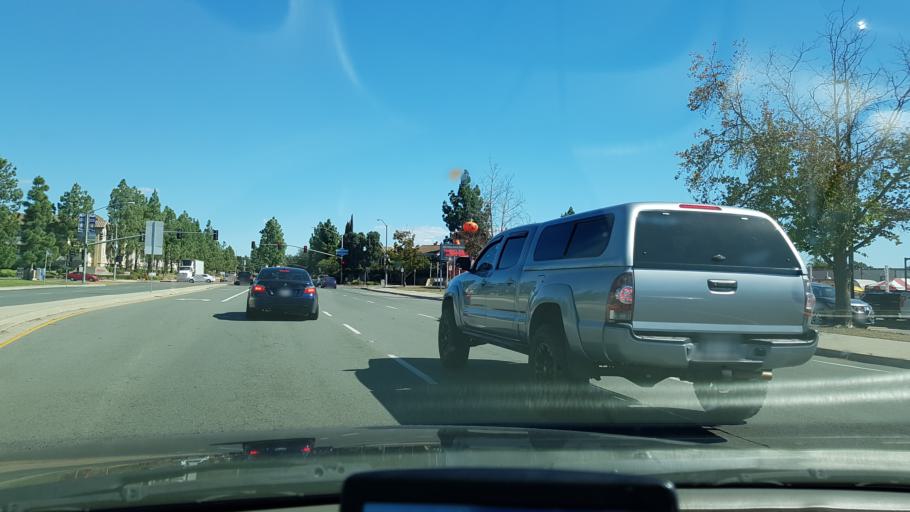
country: US
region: California
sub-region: San Diego County
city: Fairbanks Ranch
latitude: 32.9128
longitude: -117.1399
